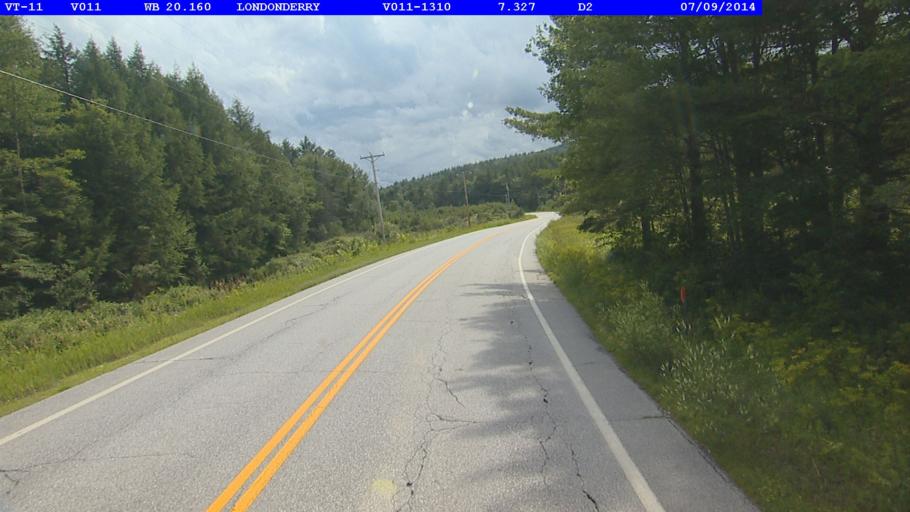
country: US
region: Vermont
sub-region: Windsor County
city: Chester
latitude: 43.2247
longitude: -72.7311
